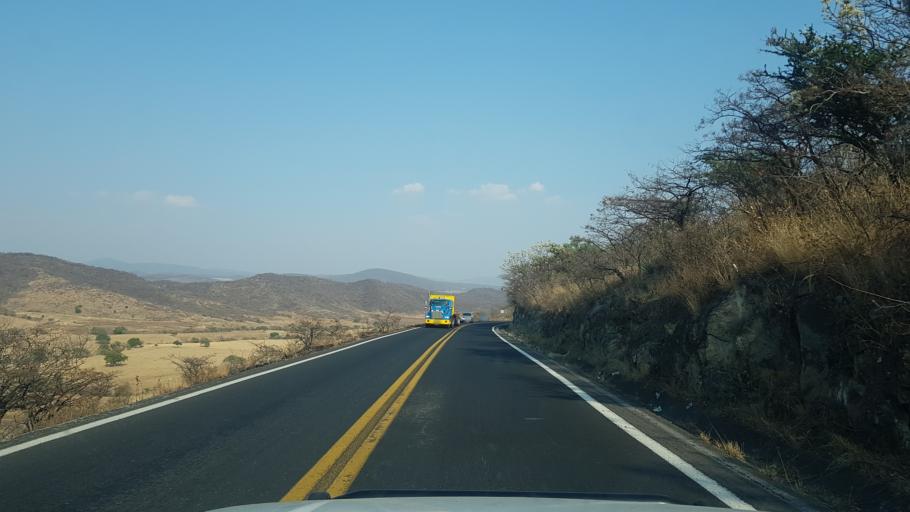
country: MX
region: Puebla
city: Calmeca
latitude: 18.6434
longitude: -98.5953
